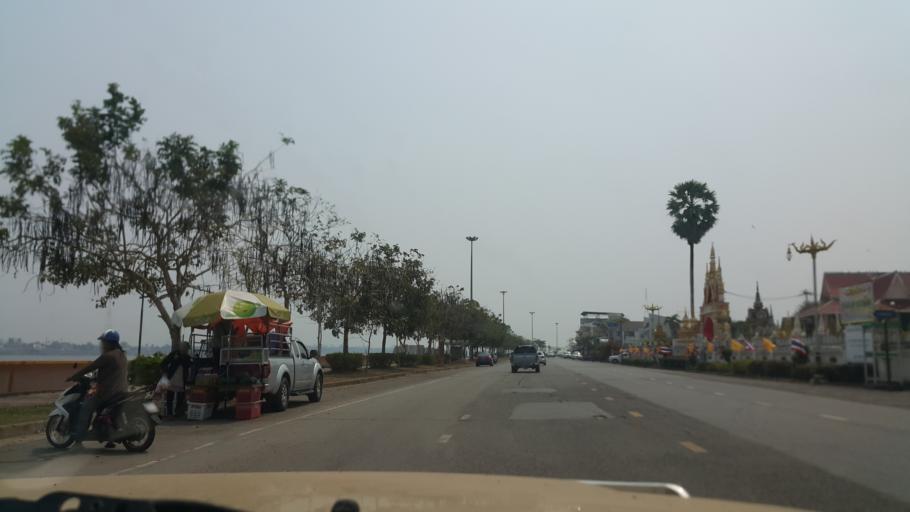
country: TH
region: Nakhon Phanom
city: Nakhon Phanom
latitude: 17.3982
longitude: 104.7908
